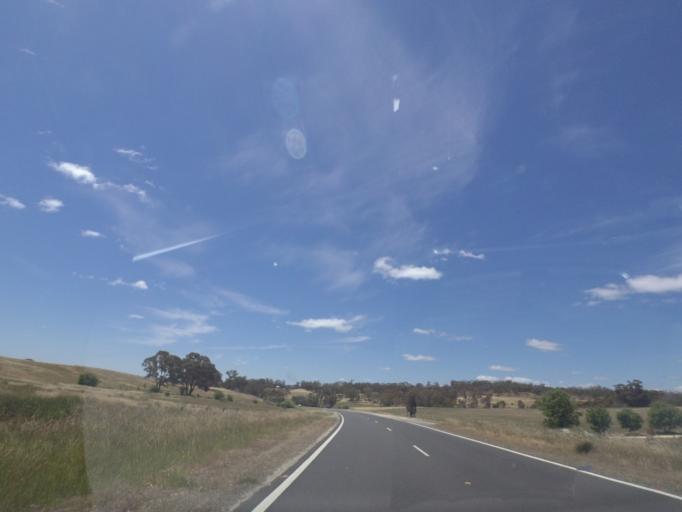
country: AU
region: Victoria
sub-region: Mount Alexander
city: Castlemaine
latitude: -37.1620
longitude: 144.1561
